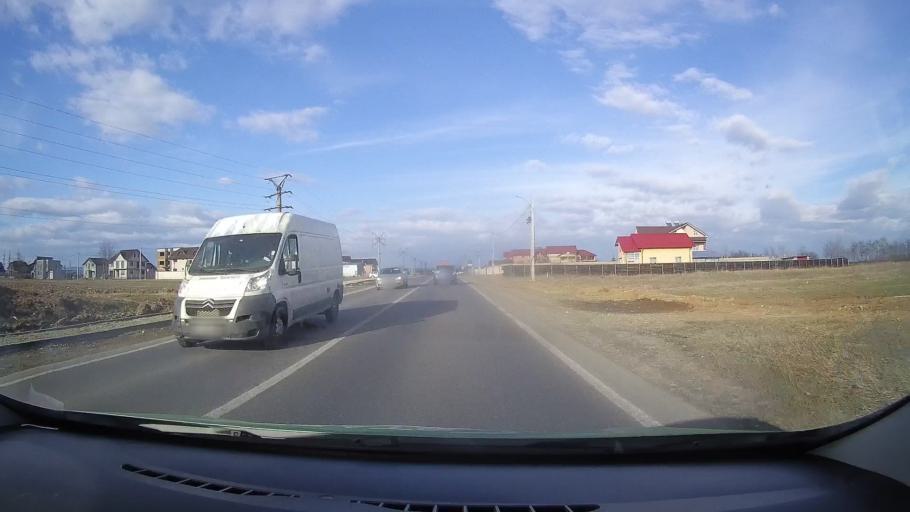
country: RO
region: Dambovita
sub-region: Comuna Ulmi
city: Viisoara
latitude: 44.8846
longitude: 25.4312
